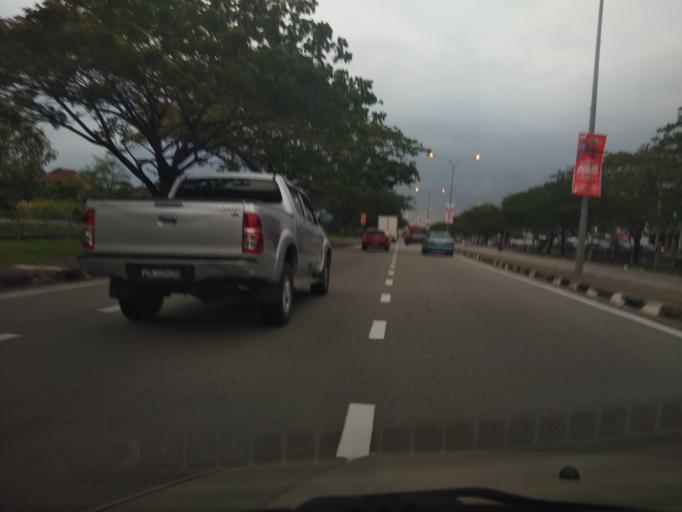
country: MY
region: Penang
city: Kepala Batas
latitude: 5.5180
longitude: 100.4478
